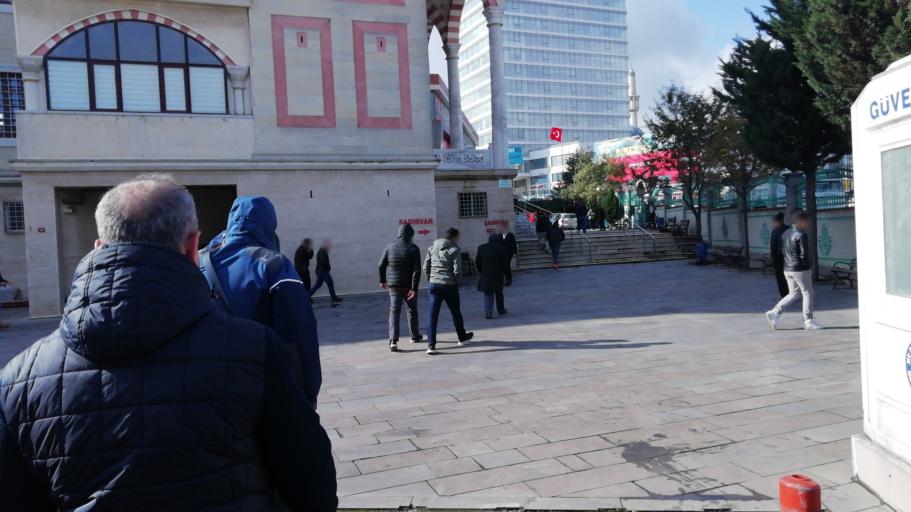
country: TR
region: Istanbul
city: Basaksehir
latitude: 41.0696
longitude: 28.8061
